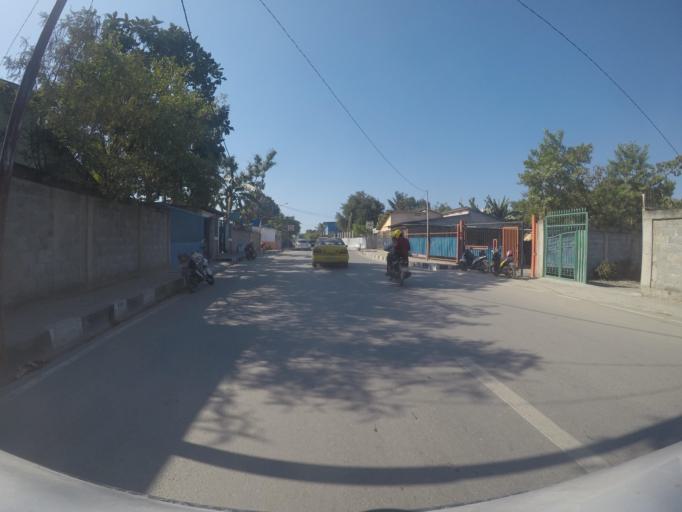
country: TL
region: Dili
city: Dili
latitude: -8.5641
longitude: 125.5558
